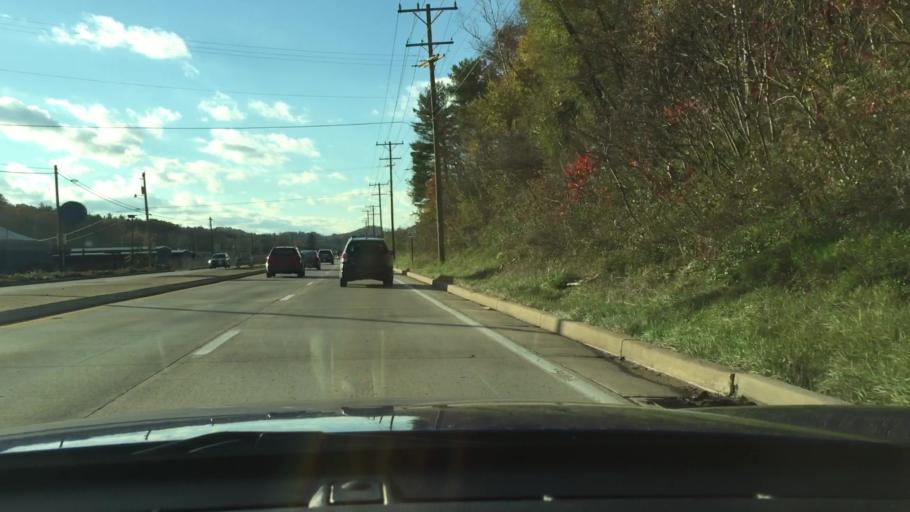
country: US
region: Pennsylvania
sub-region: Westmoreland County
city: Murrysville
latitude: 40.4262
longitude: -79.6765
